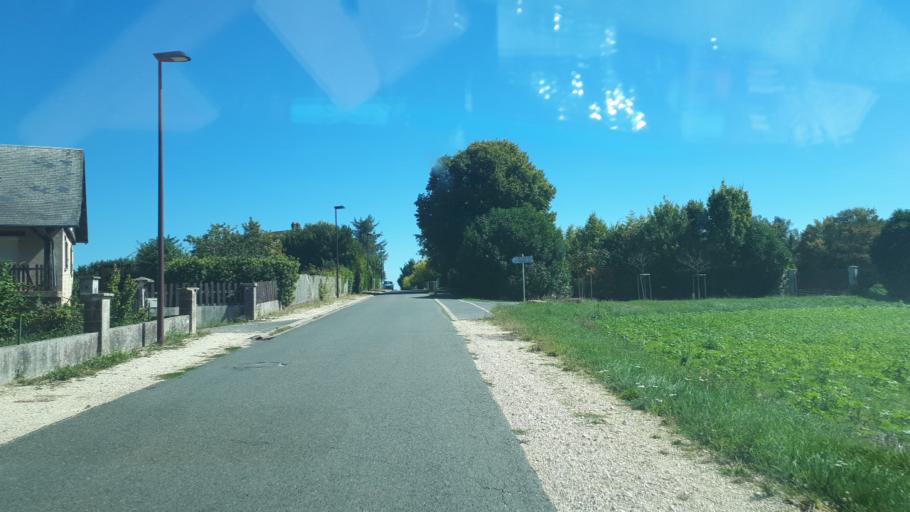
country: FR
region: Centre
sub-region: Departement du Cher
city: Rians
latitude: 47.1857
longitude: 2.6029
